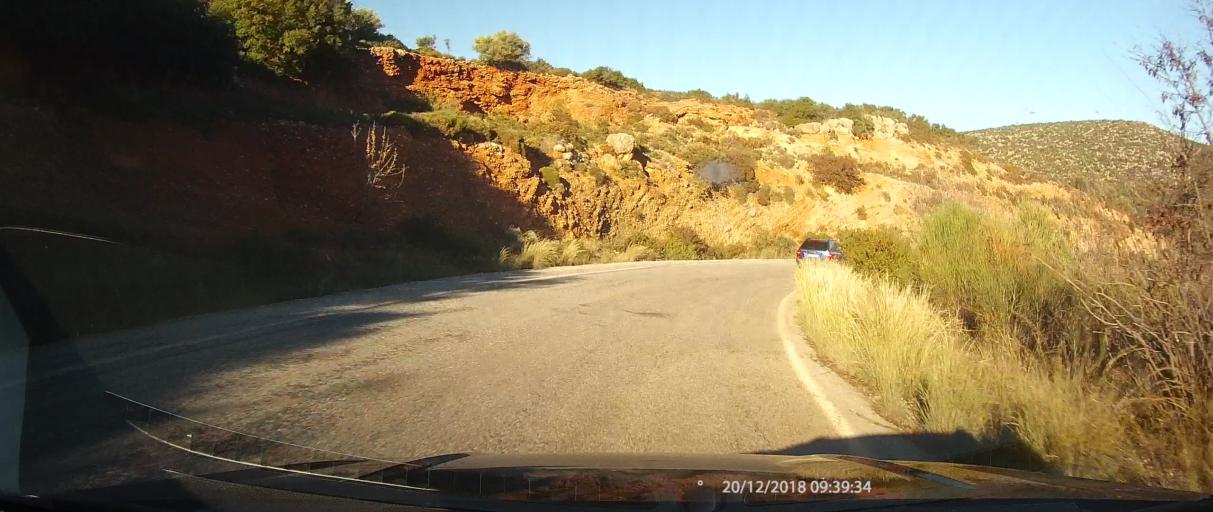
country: GR
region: Peloponnese
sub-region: Nomos Lakonias
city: Yerakion
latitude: 36.9402
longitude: 22.7738
